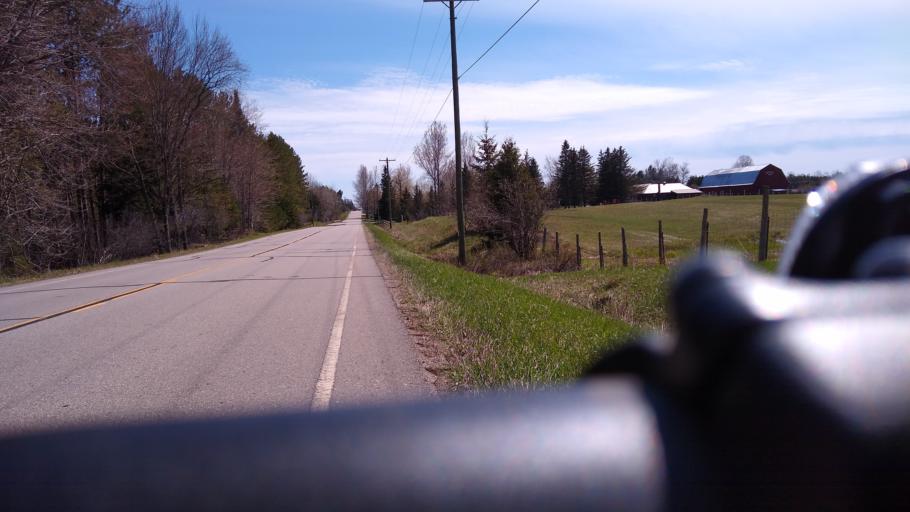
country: US
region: Michigan
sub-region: Delta County
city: Escanaba
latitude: 45.7271
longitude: -87.2025
